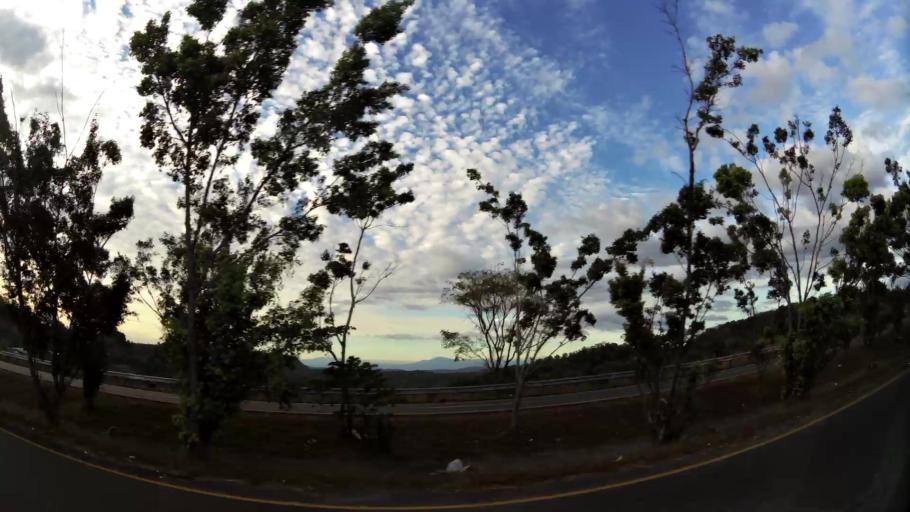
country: SV
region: Cuscatlan
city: Cojutepeque
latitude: 13.7241
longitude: -88.9021
